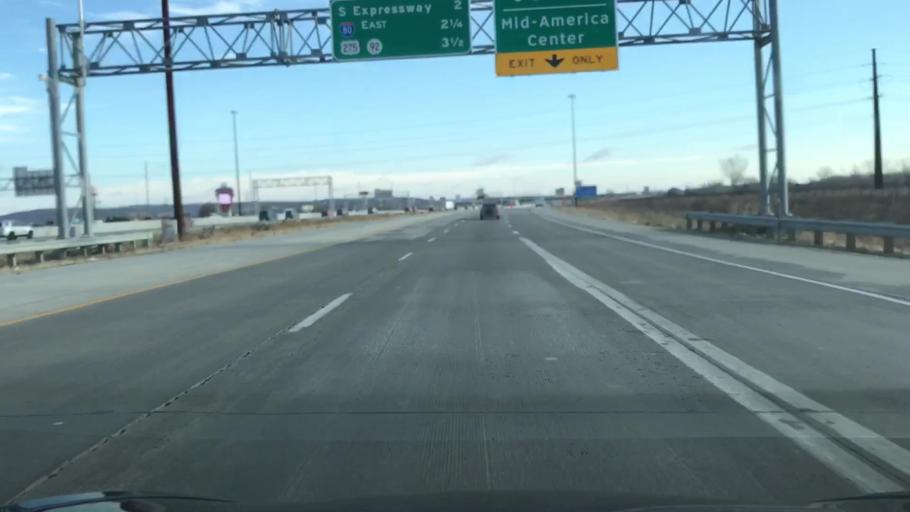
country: US
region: Iowa
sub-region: Pottawattamie County
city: Council Bluffs
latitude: 41.2321
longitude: -95.8912
